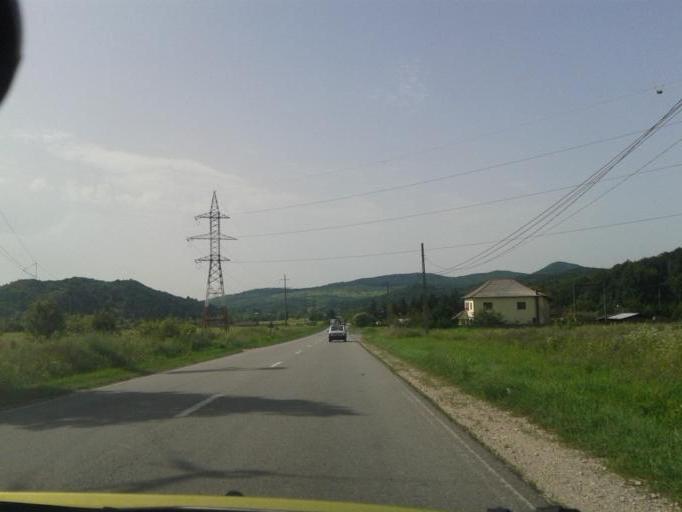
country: RO
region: Valcea
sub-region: Oras Baile Govora
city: Baile Govora
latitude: 45.0900
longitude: 24.2175
